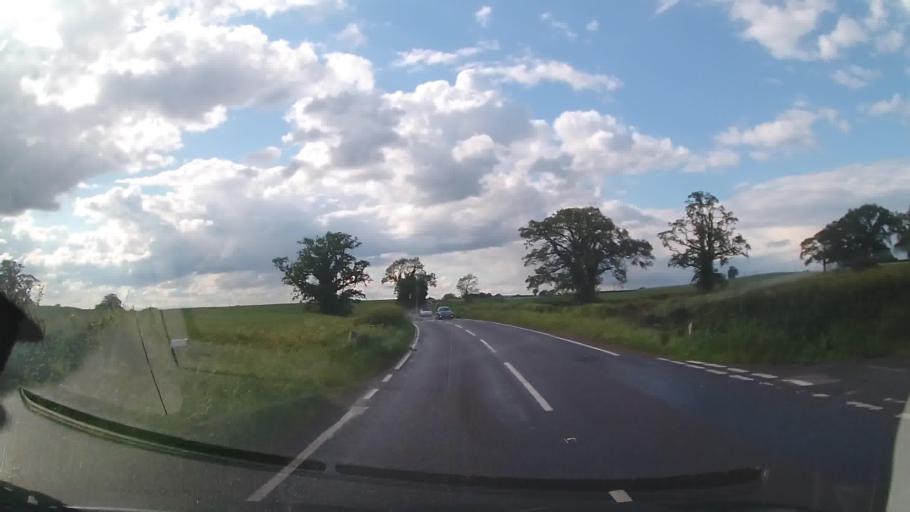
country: GB
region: England
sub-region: Shropshire
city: Withington
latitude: 52.6641
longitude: -2.6248
